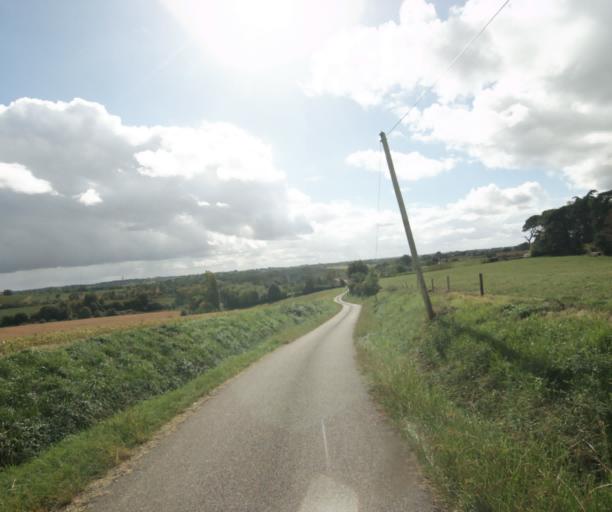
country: FR
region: Midi-Pyrenees
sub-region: Departement du Gers
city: Eauze
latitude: 43.8568
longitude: 0.0651
